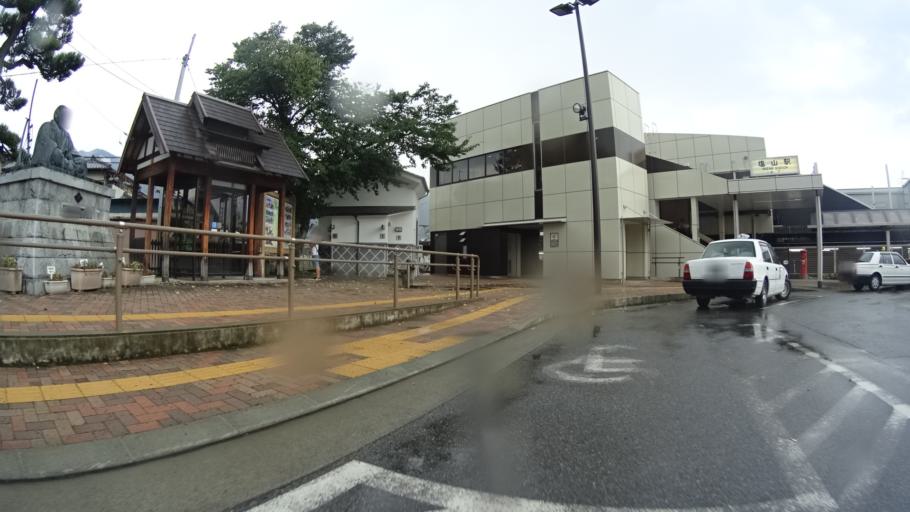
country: JP
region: Yamanashi
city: Enzan
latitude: 35.7058
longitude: 138.7345
